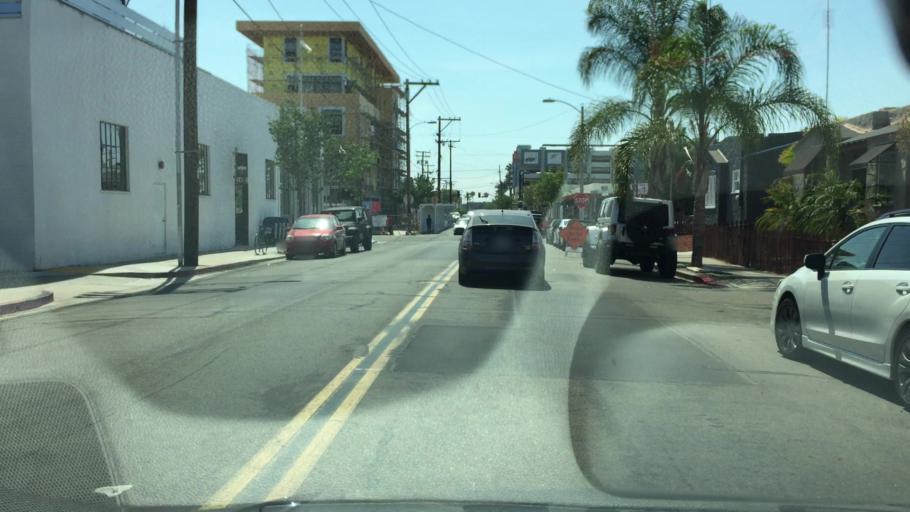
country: US
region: California
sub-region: San Diego County
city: San Diego
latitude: 32.7474
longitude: -117.1276
